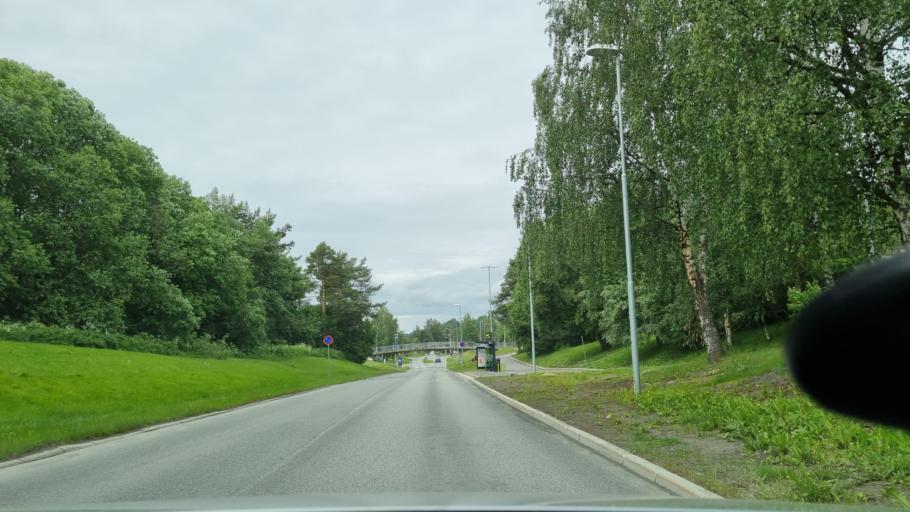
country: NO
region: Sor-Trondelag
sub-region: Melhus
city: Melhus
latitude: 63.3455
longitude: 10.3392
